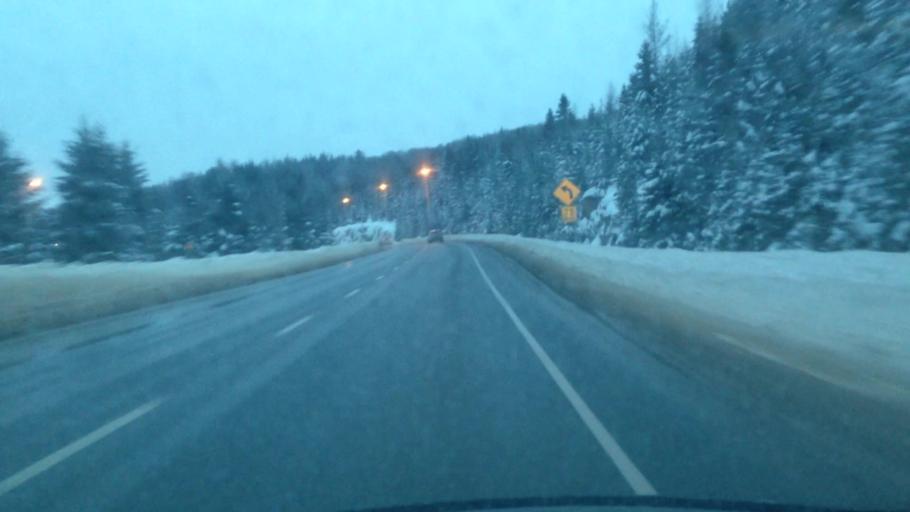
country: CA
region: Quebec
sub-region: Laurentides
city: Sainte-Agathe-des-Monts
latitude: 46.1214
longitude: -74.4321
